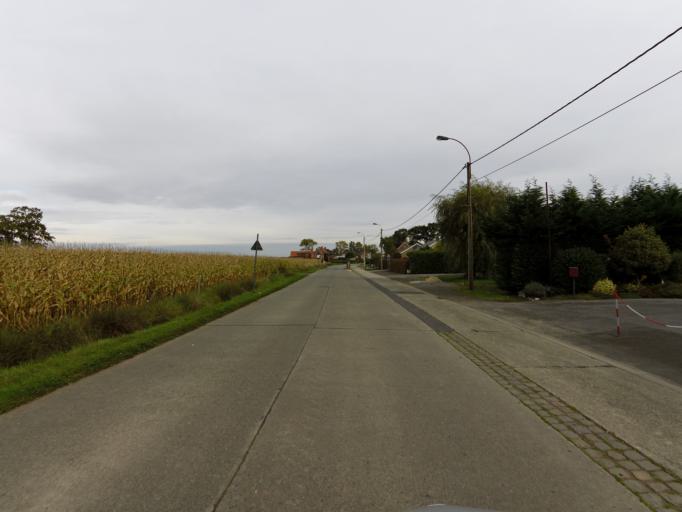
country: BE
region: Flanders
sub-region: Provincie West-Vlaanderen
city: Ichtegem
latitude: 51.1161
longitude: 3.0681
